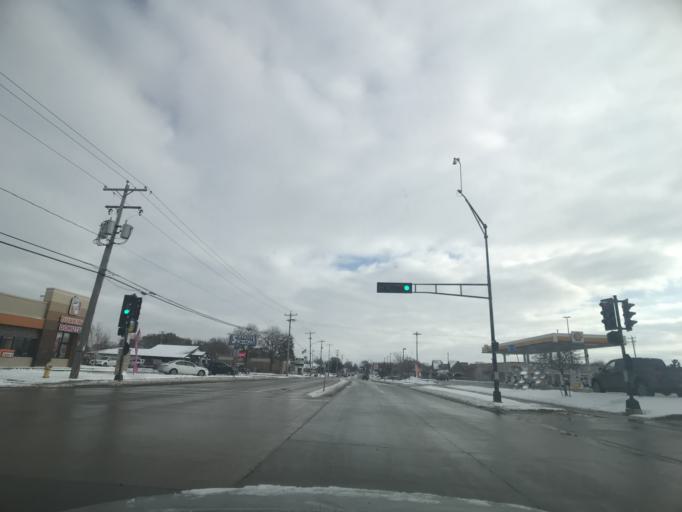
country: US
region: Wisconsin
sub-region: Brown County
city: De Pere
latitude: 44.4513
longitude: -88.0859
